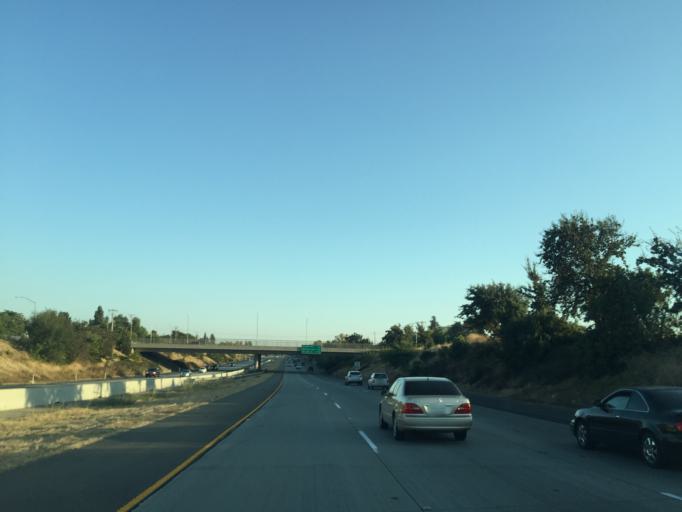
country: US
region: California
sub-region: Fresno County
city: Fresno
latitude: 36.7889
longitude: -119.7491
